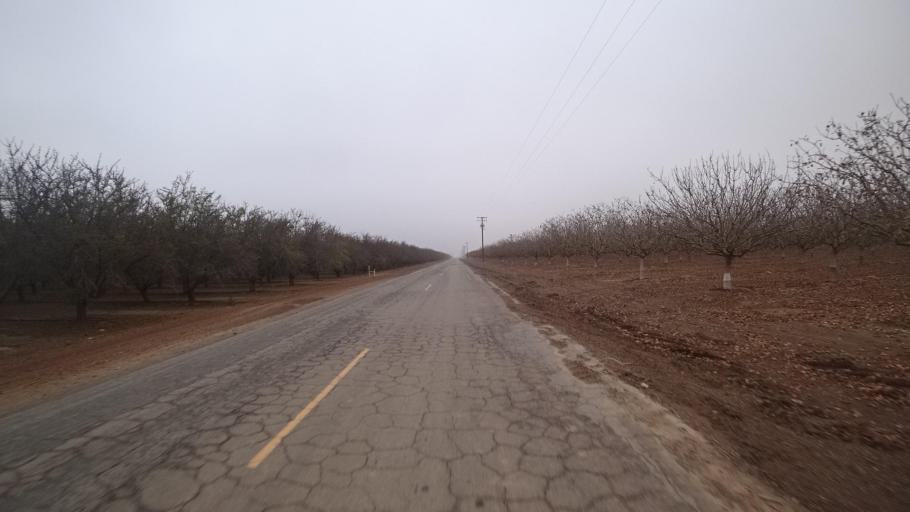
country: US
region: California
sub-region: Kern County
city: Wasco
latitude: 35.5721
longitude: -119.4824
